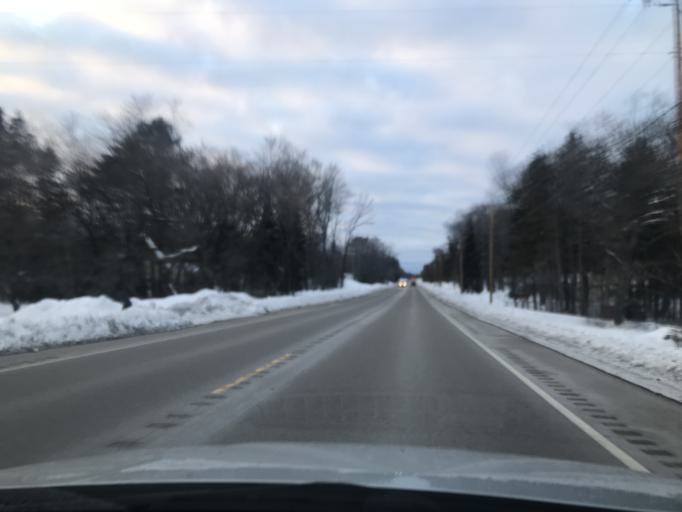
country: US
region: Wisconsin
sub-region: Marinette County
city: Marinette
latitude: 45.1548
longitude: -87.7107
